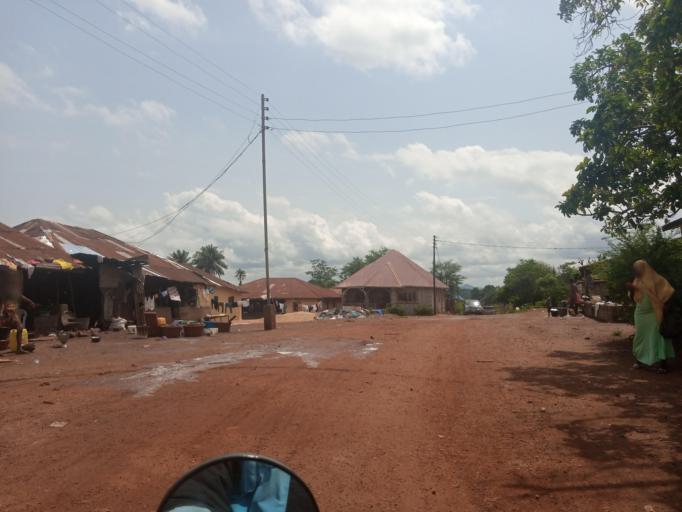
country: SL
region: Southern Province
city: Bo
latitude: 7.9686
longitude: -11.7350
